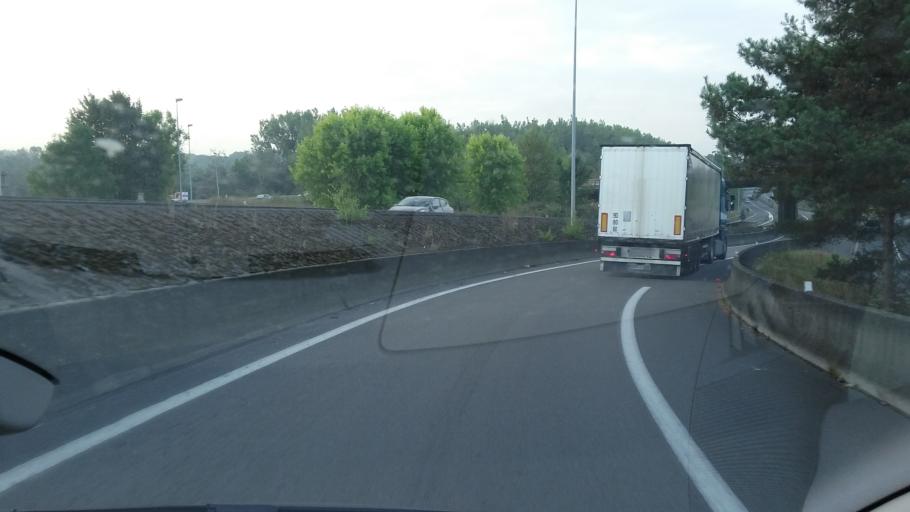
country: FR
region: Champagne-Ardenne
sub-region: Departement des Ardennes
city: La Francheville
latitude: 49.7360
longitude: 4.7215
